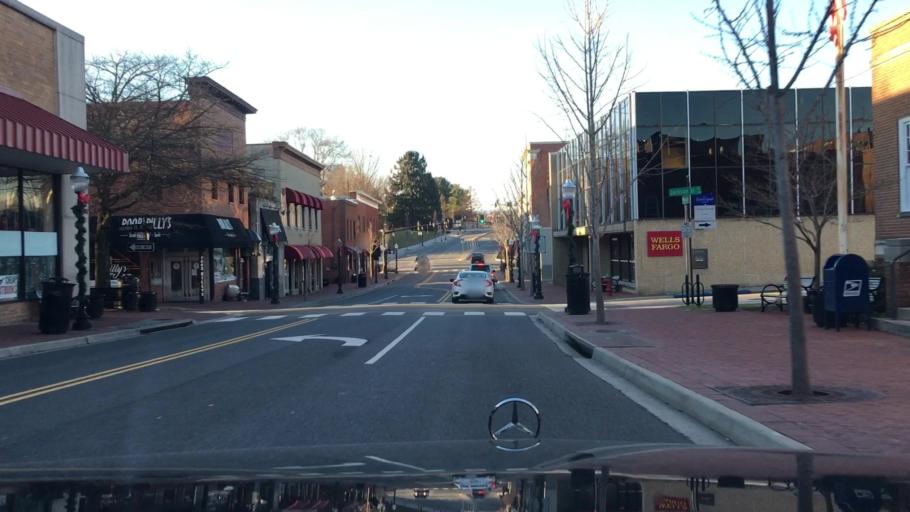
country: US
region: Virginia
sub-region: Montgomery County
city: Blacksburg
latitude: 37.2299
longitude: -80.4145
